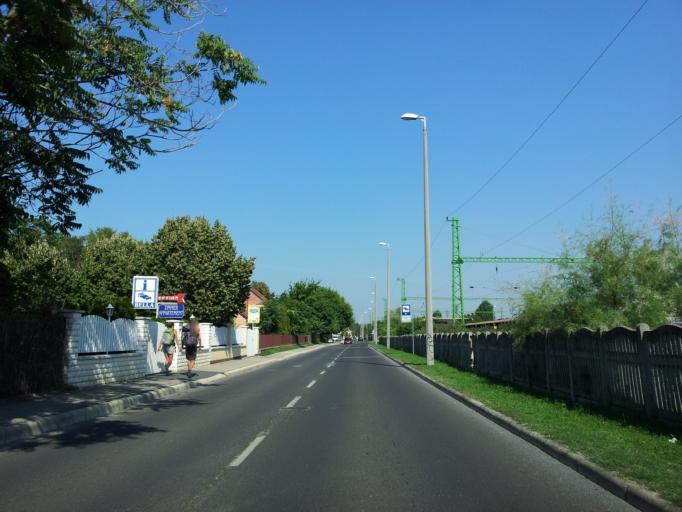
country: HU
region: Somogy
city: Siofok
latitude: 46.9076
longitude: 18.0517
